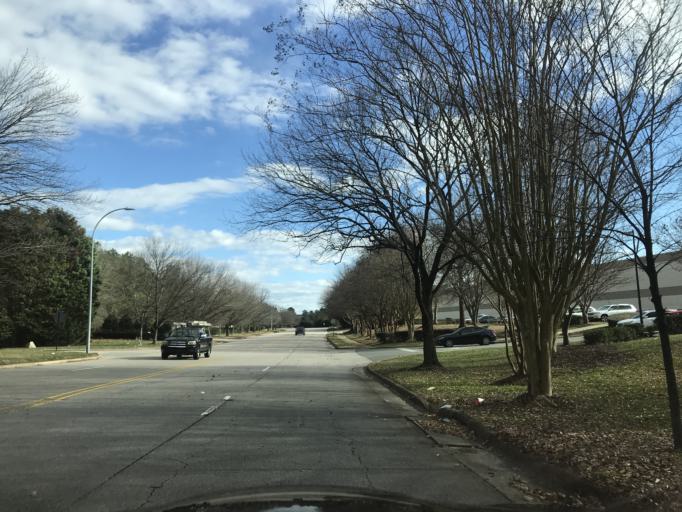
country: US
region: North Carolina
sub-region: Wake County
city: Cary
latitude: 35.7588
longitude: -78.7385
